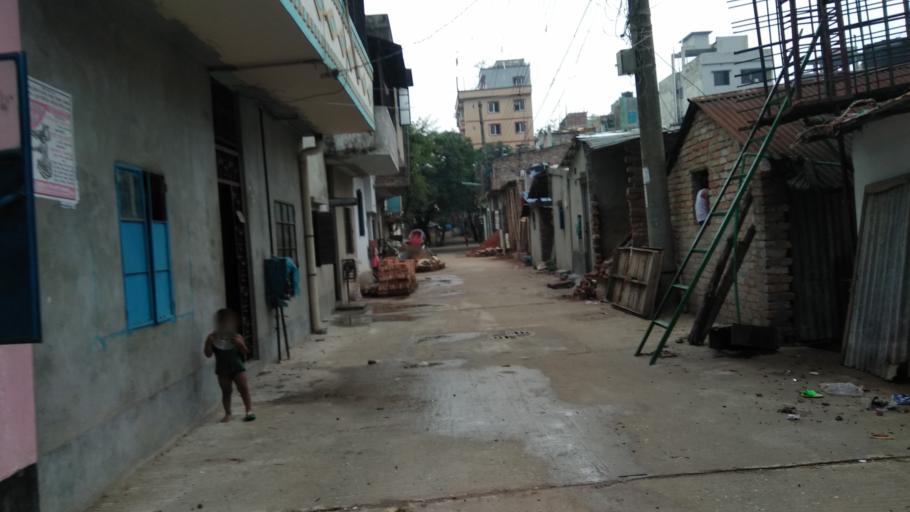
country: BD
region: Dhaka
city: Tungi
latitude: 23.8244
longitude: 90.3702
